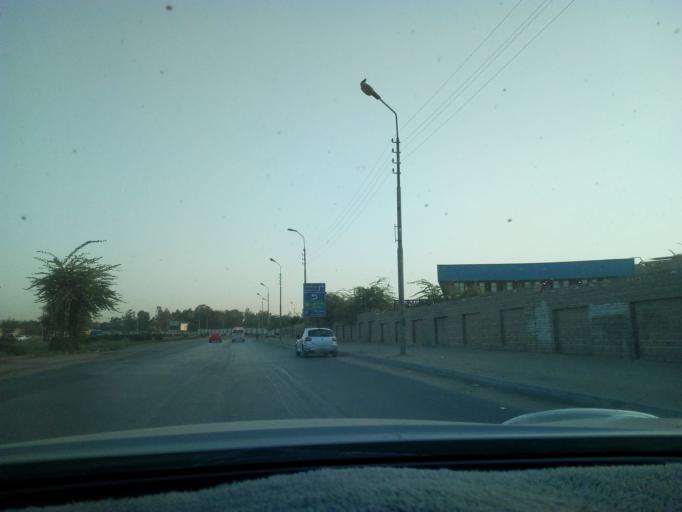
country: EG
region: Muhafazat al Qalyubiyah
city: Al Khankah
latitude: 30.1192
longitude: 31.3638
